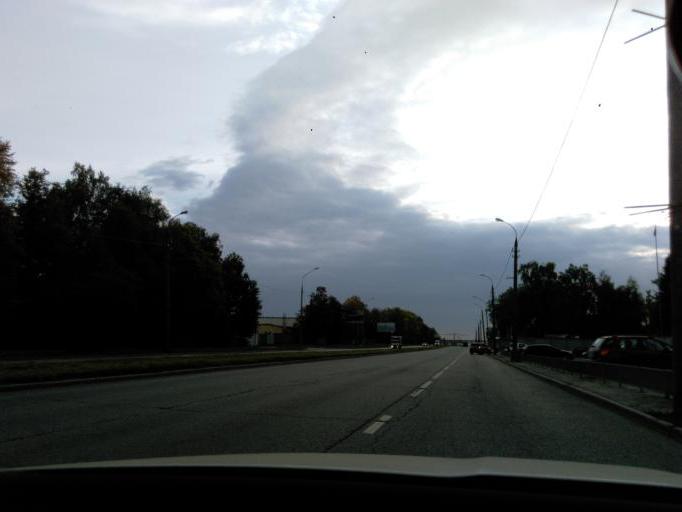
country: RU
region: Moskovskaya
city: Novopodrezkovo
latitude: 55.9798
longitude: 37.3991
